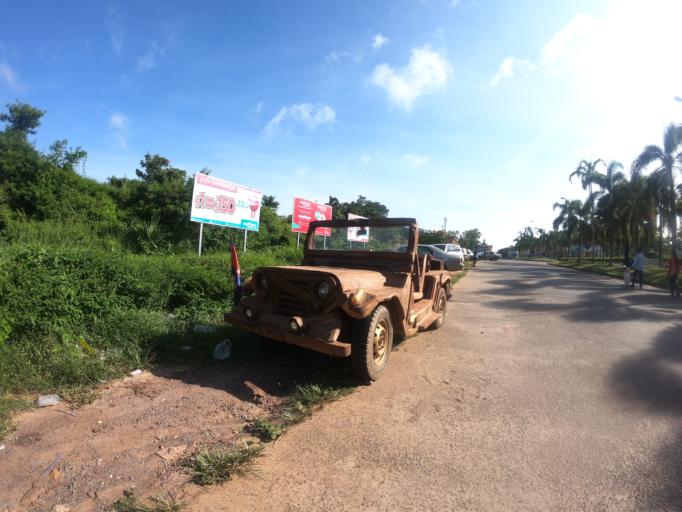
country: TH
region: Surin
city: Kap Choeng
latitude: 14.4329
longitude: 103.6991
